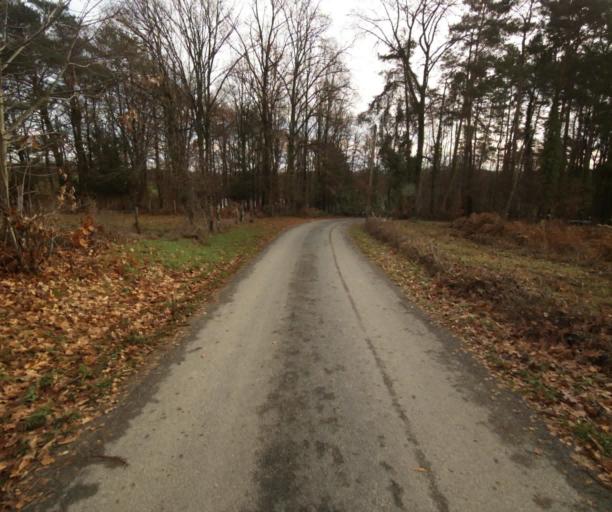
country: FR
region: Limousin
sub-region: Departement de la Correze
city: Chameyrat
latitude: 45.2538
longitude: 1.6859
